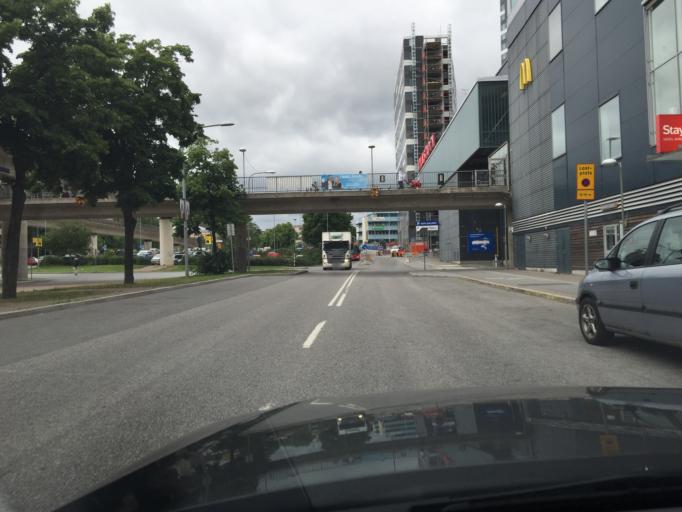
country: SE
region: Stockholm
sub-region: Stockholms Kommun
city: Kista
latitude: 59.4036
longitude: 17.9428
